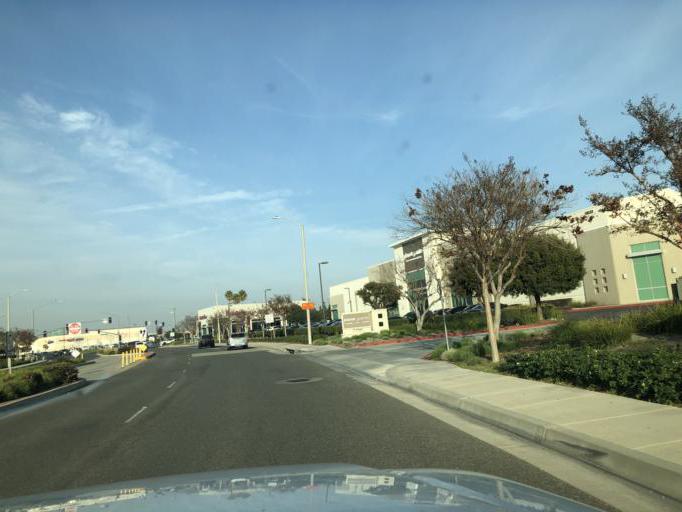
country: US
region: California
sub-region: Orange County
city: Fountain Valley
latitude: 33.7005
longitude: -117.9353
